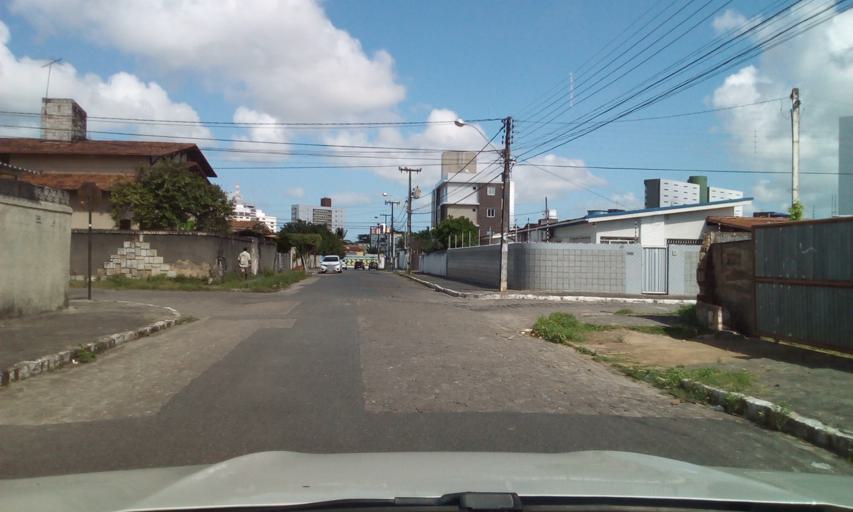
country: BR
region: Paraiba
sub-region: Joao Pessoa
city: Joao Pessoa
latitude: -7.1157
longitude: -34.8650
